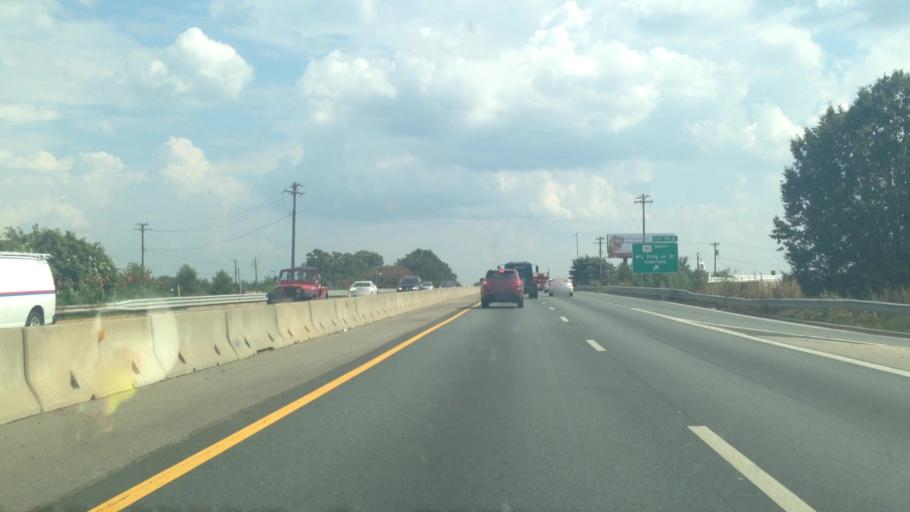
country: US
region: North Carolina
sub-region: Forsyth County
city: Winston-Salem
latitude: 36.1098
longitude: -80.2366
